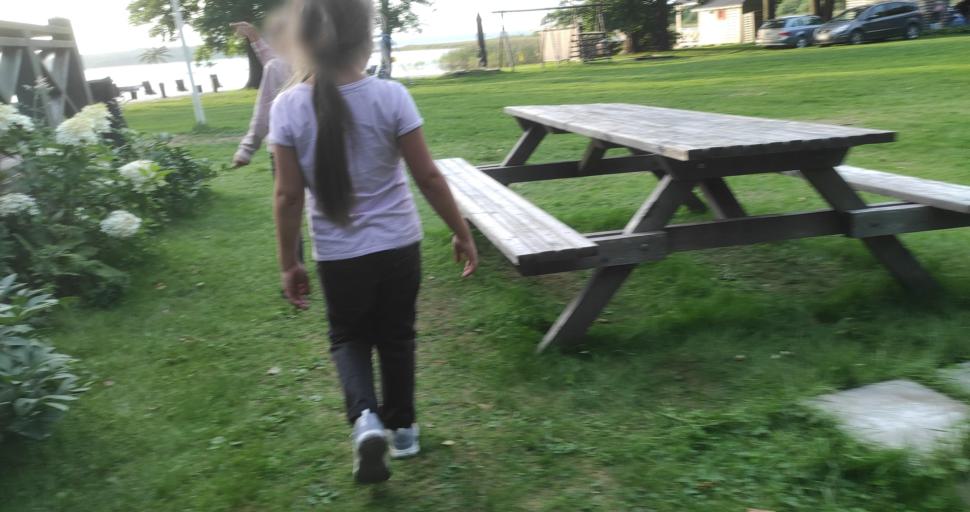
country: LV
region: Kuldigas Rajons
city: Kuldiga
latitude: 57.1230
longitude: 22.1898
